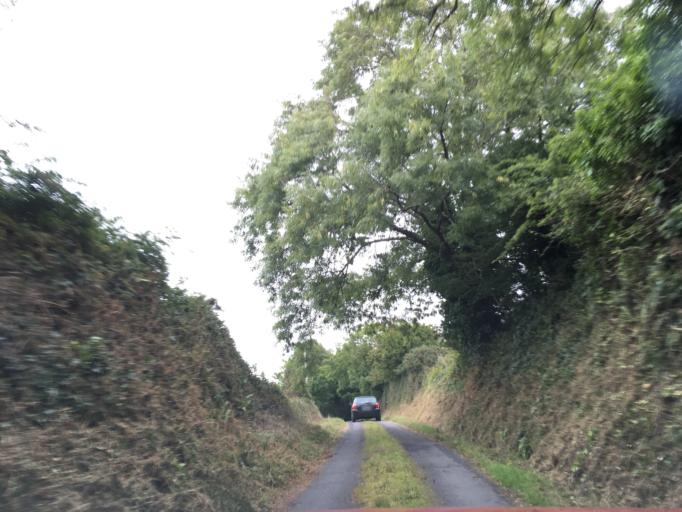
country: IE
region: Munster
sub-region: County Limerick
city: Askeaton
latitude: 52.7163
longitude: -9.0609
